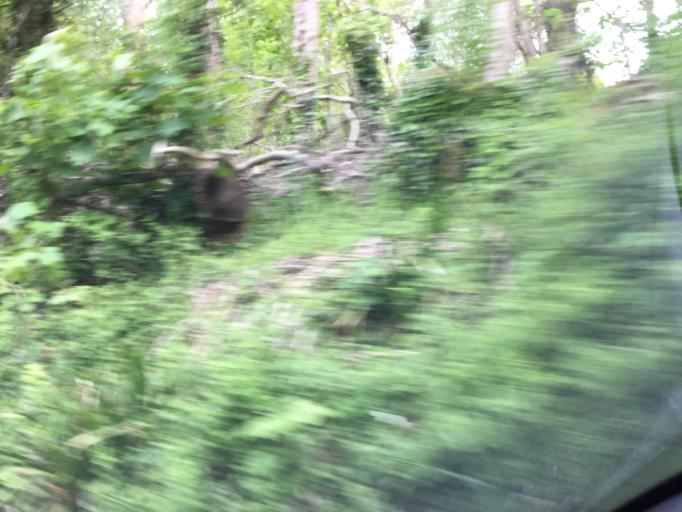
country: GB
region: England
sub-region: Bath and North East Somerset
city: Freshford
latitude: 51.3734
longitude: -2.3126
